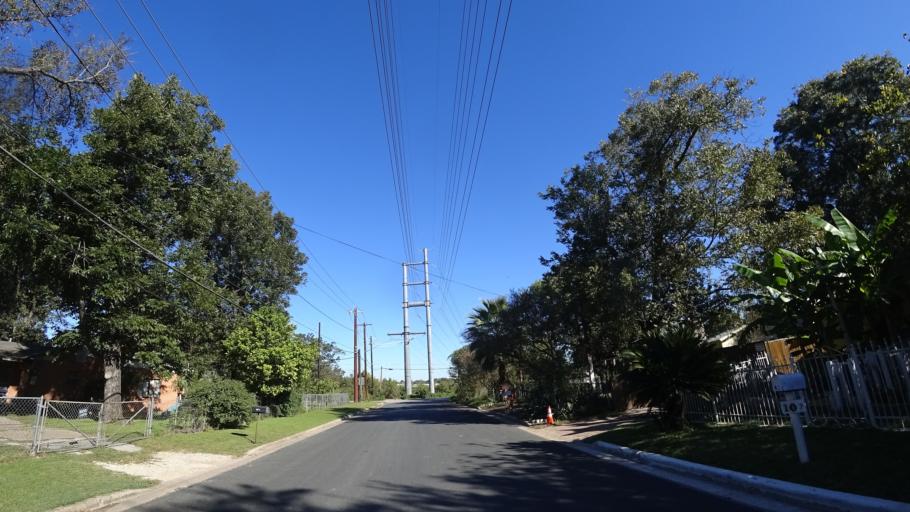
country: US
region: Texas
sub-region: Travis County
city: Austin
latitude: 30.2442
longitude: -97.6892
